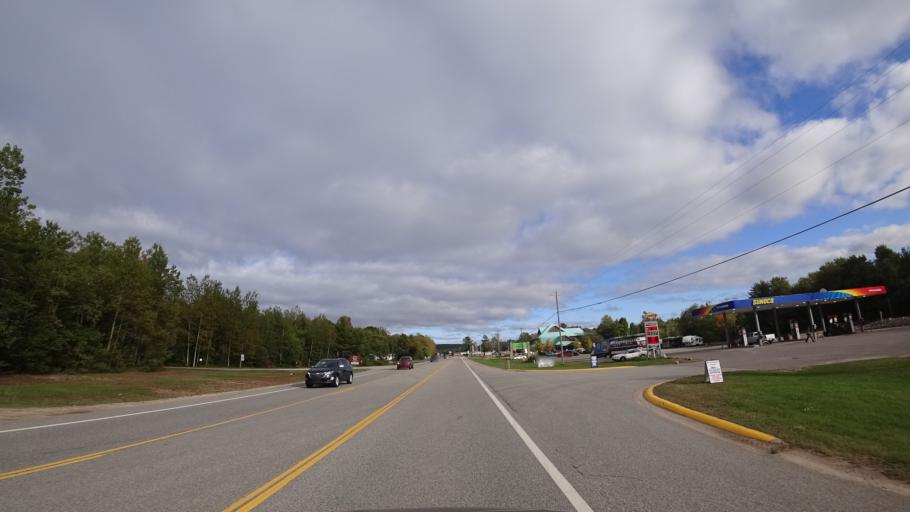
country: US
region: Michigan
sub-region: Alger County
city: Munising
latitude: 46.4383
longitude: -86.7092
